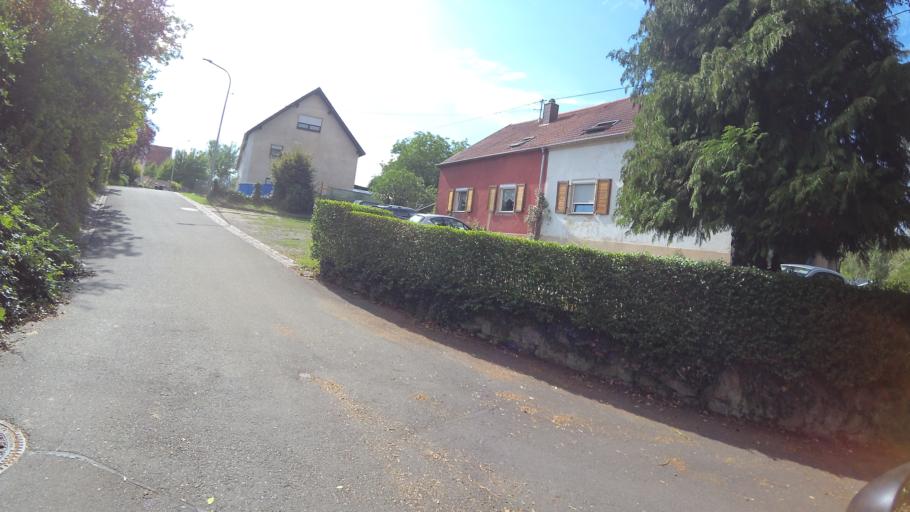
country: DE
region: Saarland
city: Gersheim
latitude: 49.1344
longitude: 7.2047
